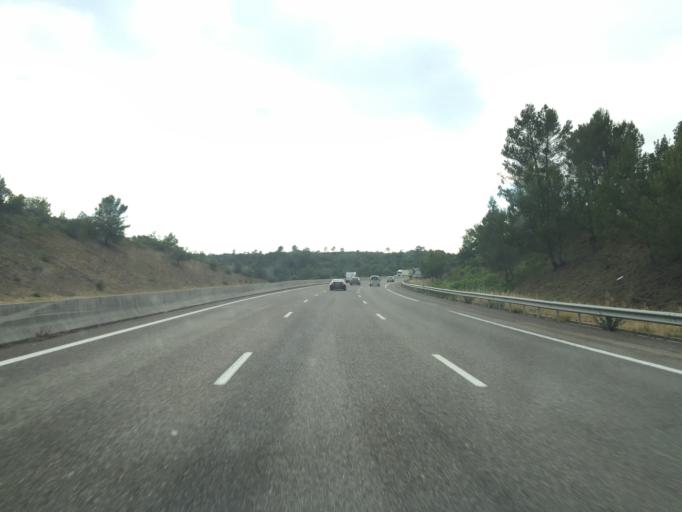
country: FR
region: Provence-Alpes-Cote d'Azur
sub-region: Departement du Var
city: Tourves
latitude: 43.4378
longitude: 5.9099
